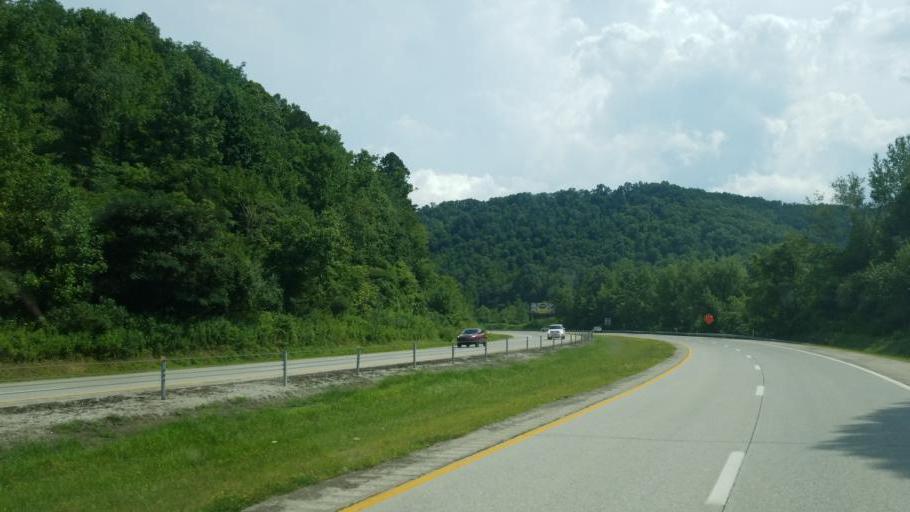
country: US
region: West Virginia
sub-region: Boone County
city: Madison
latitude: 38.1593
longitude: -81.8546
